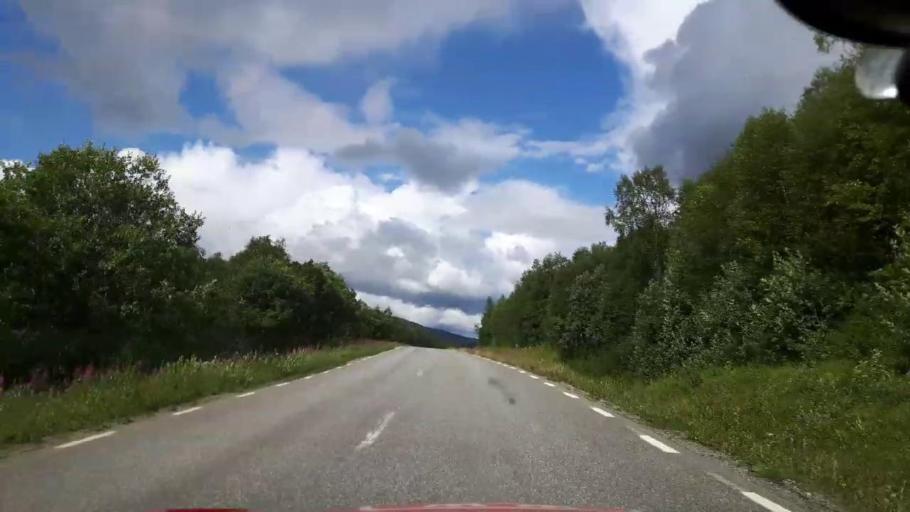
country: NO
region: Nordland
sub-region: Hattfjelldal
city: Hattfjelldal
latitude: 65.0537
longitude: 14.7345
